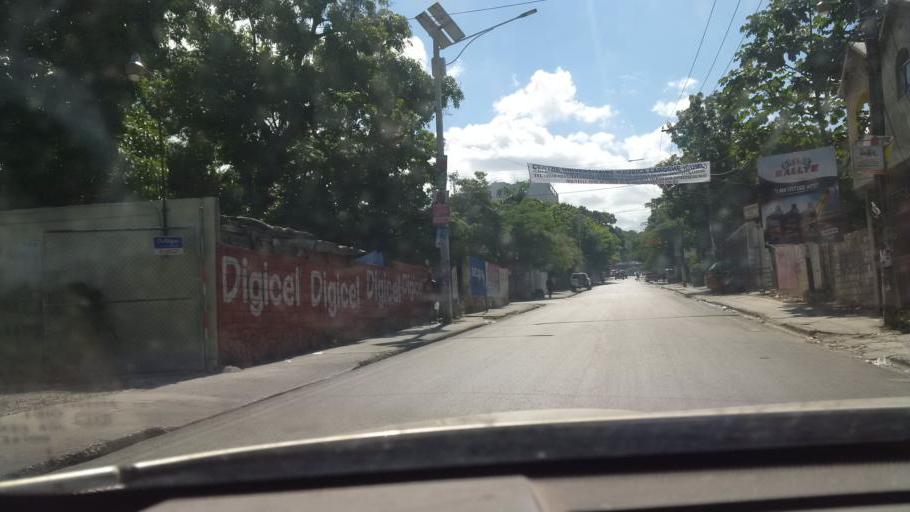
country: HT
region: Ouest
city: Port-au-Prince
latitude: 18.5337
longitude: -72.3273
